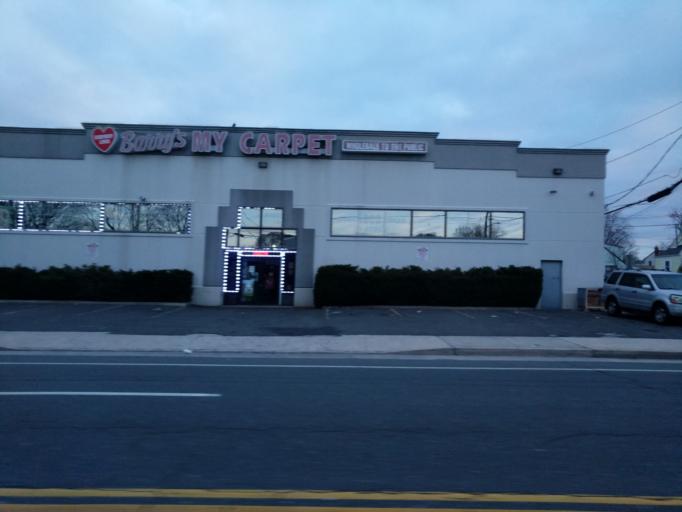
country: US
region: New York
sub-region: Nassau County
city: Valley Stream
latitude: 40.6736
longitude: -73.7251
